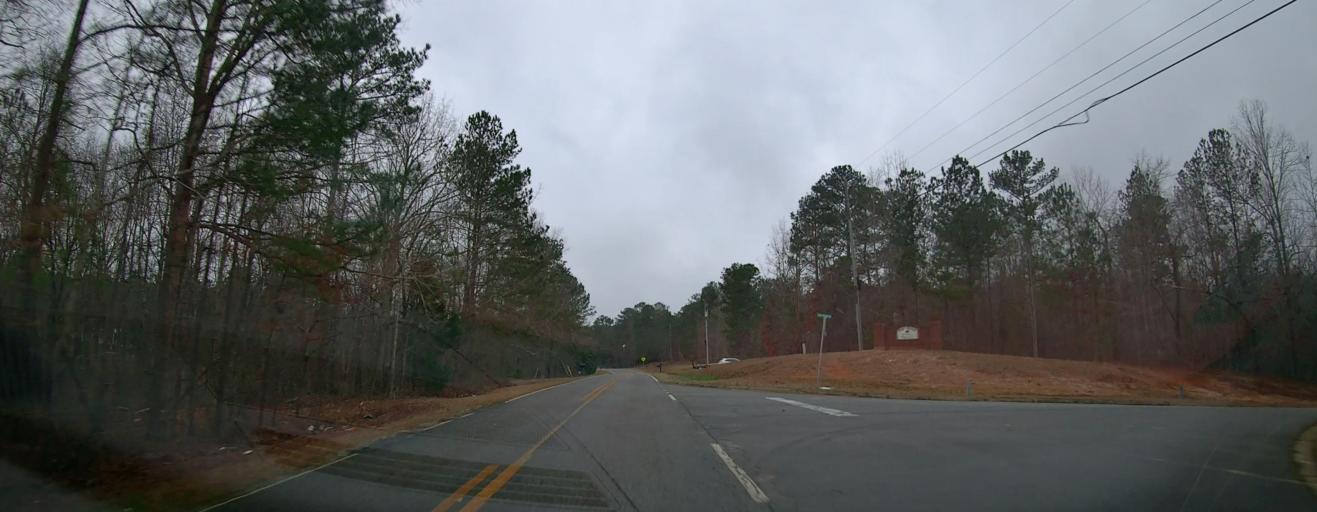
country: US
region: Georgia
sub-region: Lamar County
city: Barnesville
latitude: 33.0674
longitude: -84.1222
